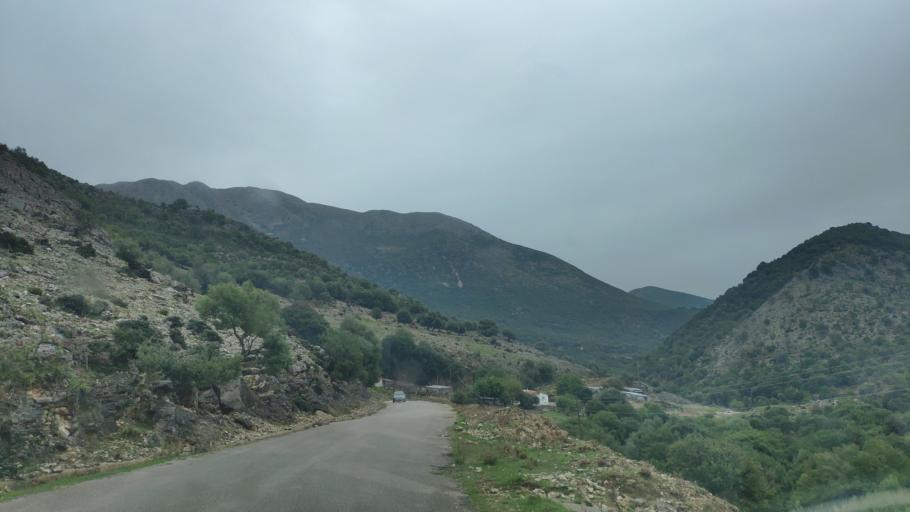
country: GR
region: Epirus
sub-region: Nomos Thesprotias
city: Paramythia
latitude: 39.3846
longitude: 20.6262
